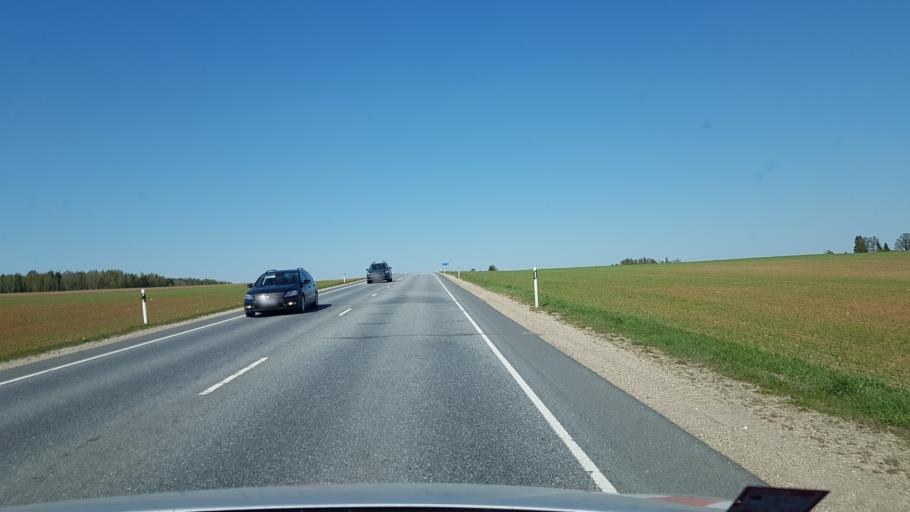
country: EE
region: Tartu
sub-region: UElenurme vald
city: Ulenurme
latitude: 58.2661
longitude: 26.6932
